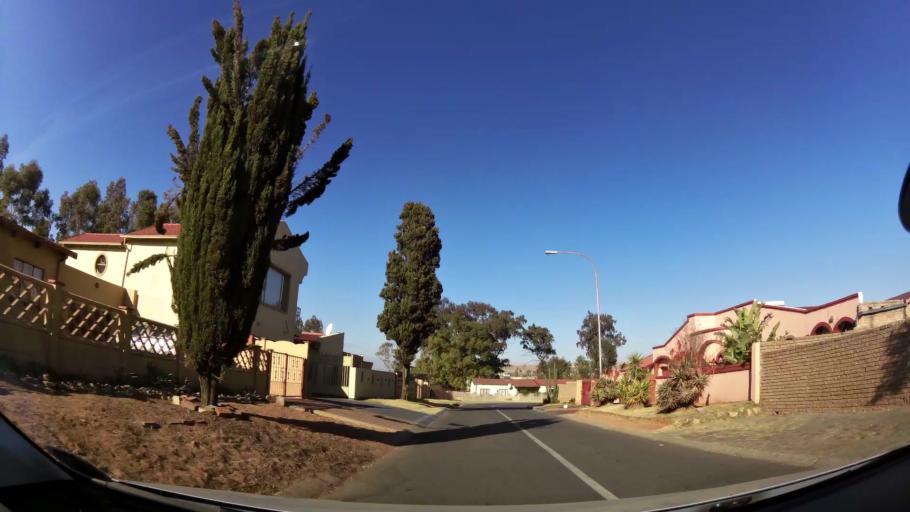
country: ZA
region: Gauteng
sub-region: City of Johannesburg Metropolitan Municipality
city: Johannesburg
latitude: -26.2081
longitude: 27.9636
